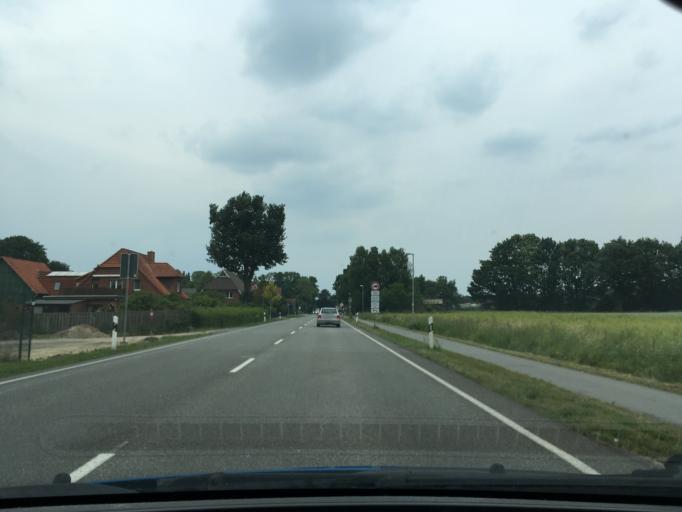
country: DE
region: Lower Saxony
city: Wenzendorf
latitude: 53.3753
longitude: 9.8039
